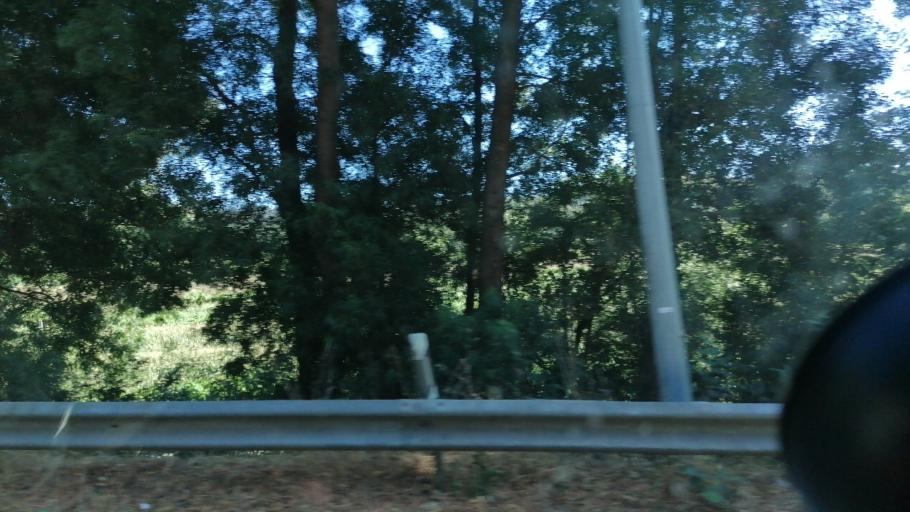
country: PT
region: Porto
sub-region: Santo Tirso
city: Santo Tirso
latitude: 41.3395
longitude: -8.5136
